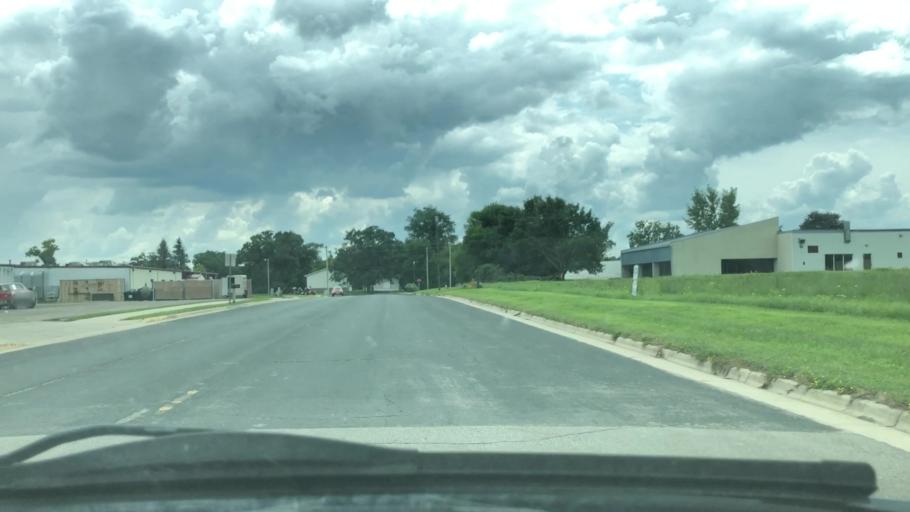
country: US
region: Minnesota
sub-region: Olmsted County
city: Stewartville
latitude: 43.8645
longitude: -92.4900
